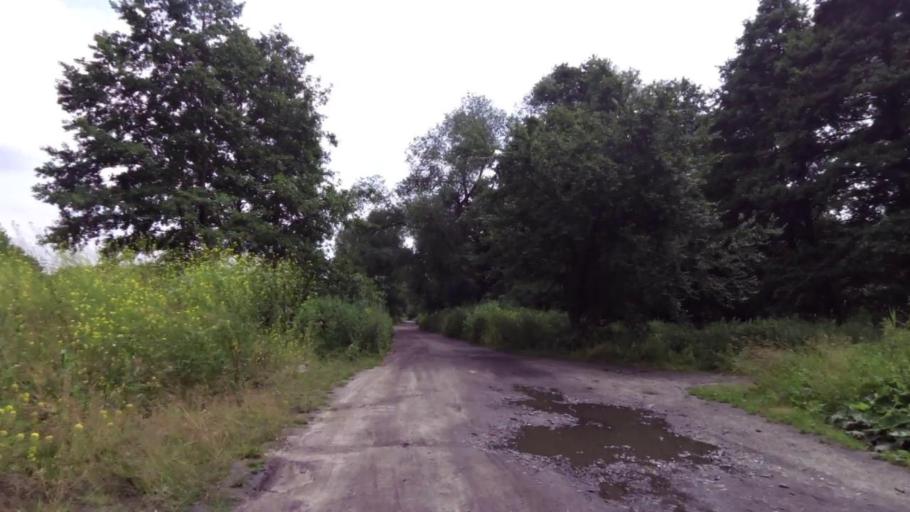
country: PL
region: West Pomeranian Voivodeship
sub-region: Szczecin
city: Szczecin
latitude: 53.4059
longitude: 14.6706
